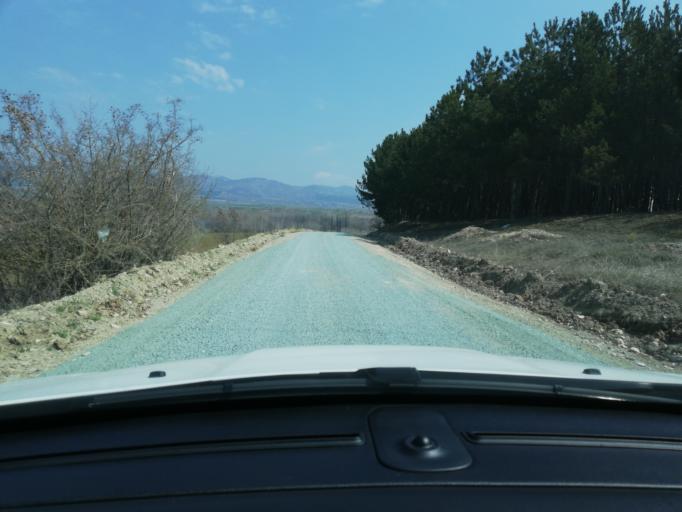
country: TR
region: Kastamonu
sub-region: Cide
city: Kastamonu
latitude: 41.4677
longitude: 33.7764
